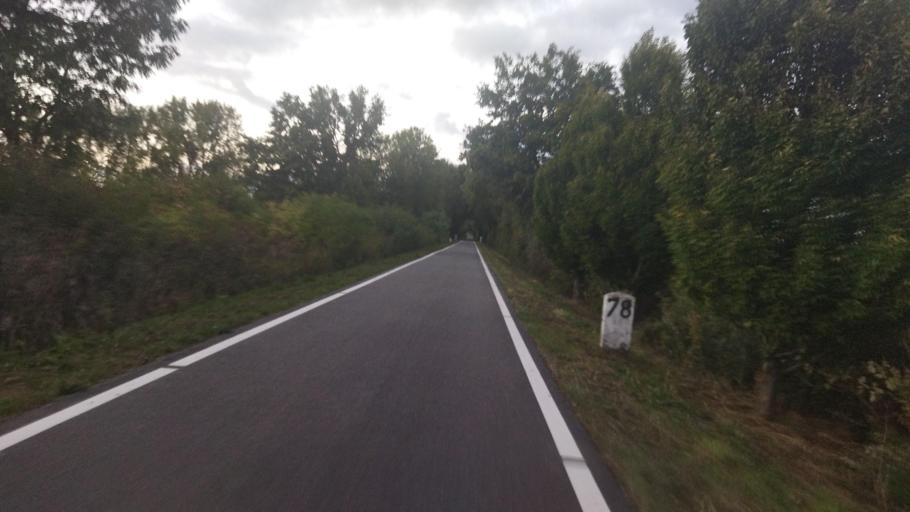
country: DE
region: North Rhine-Westphalia
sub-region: Regierungsbezirk Munster
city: Horstmar
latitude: 52.0735
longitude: 7.3208
